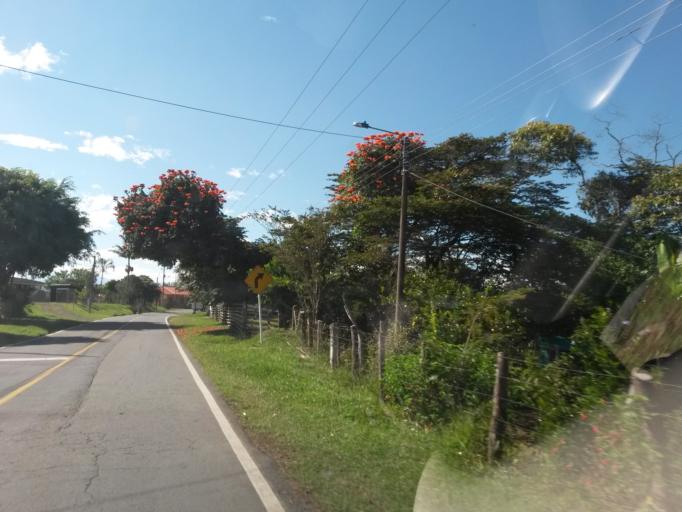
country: CO
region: Cauca
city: Morales
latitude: 2.7486
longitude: -76.6243
